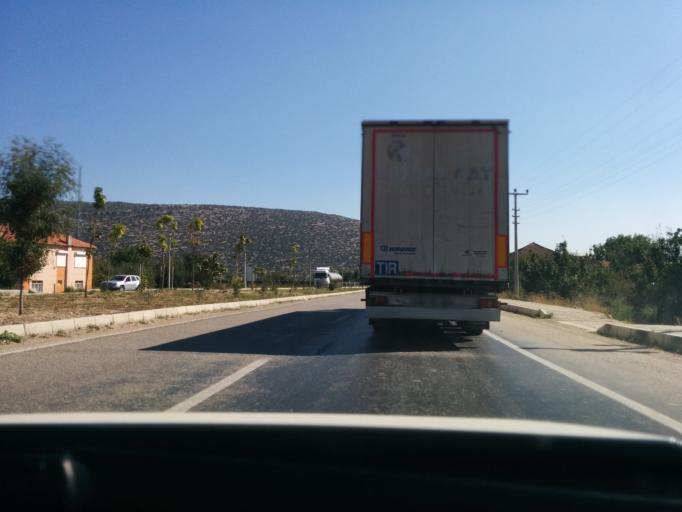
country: TR
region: Antalya
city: Korkuteli
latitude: 37.0520
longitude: 30.2369
